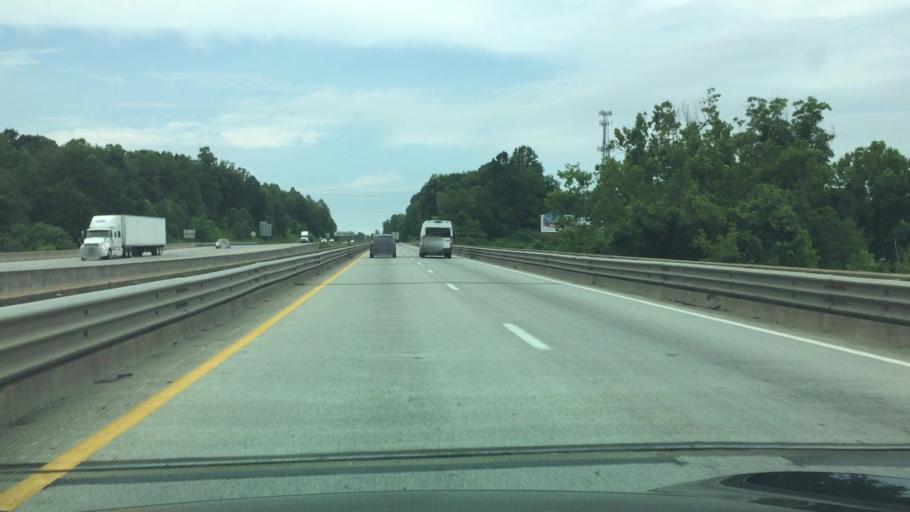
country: US
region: North Carolina
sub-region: Yadkin County
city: Jonesville
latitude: 36.2503
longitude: -80.8208
